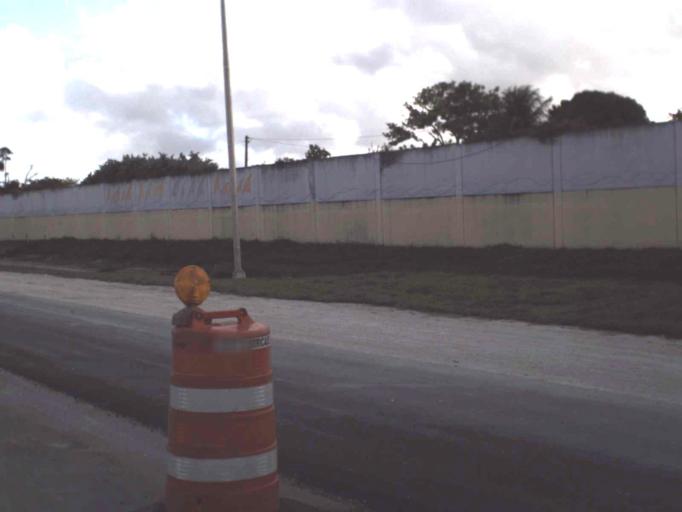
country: US
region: Florida
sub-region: Miami-Dade County
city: Norland
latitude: 25.9380
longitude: -80.2190
